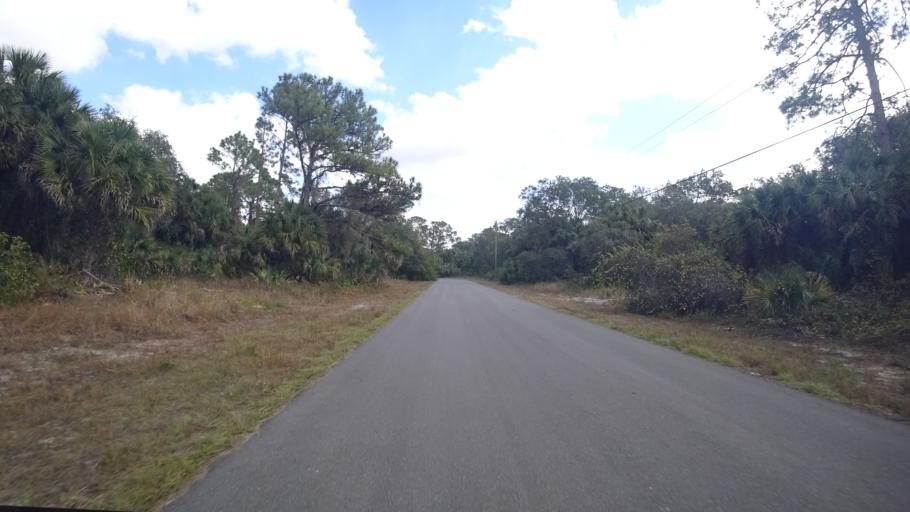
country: US
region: Florida
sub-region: Charlotte County
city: Port Charlotte
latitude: 27.0348
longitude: -82.1356
